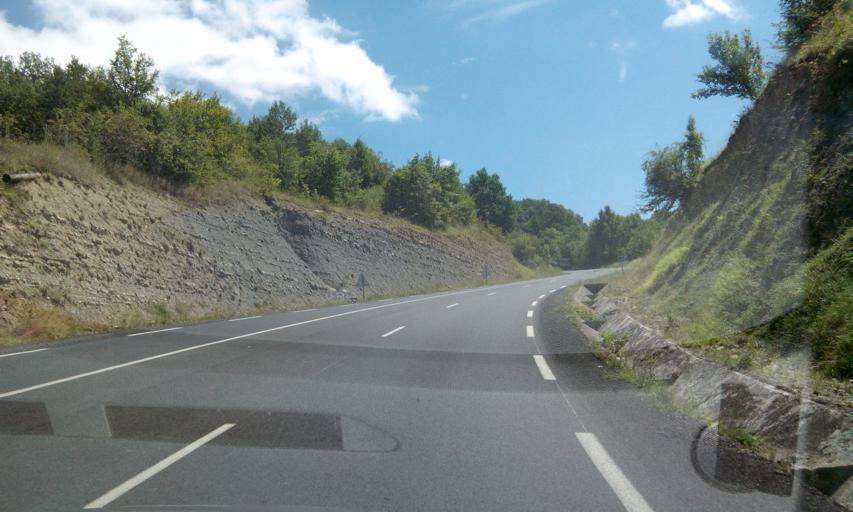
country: FR
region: Limousin
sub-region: Departement de la Correze
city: Meyssac
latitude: 45.0728
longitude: 1.6249
